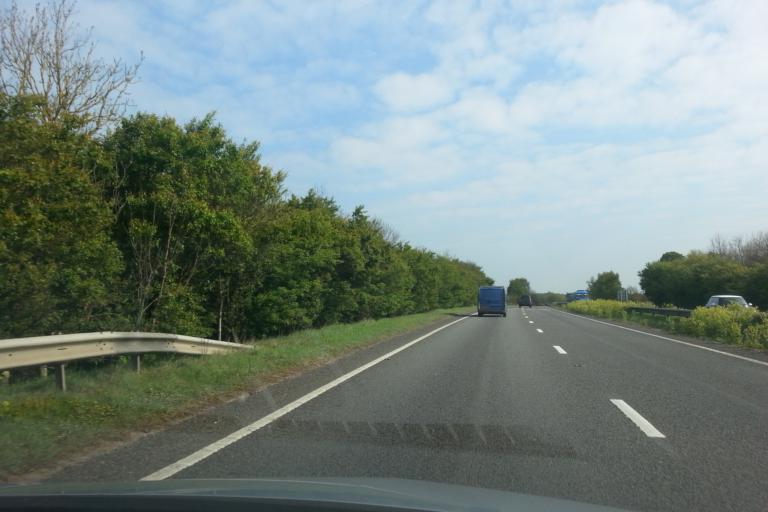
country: GB
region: England
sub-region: Suffolk
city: Kesgrave
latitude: 52.0378
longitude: 1.2605
